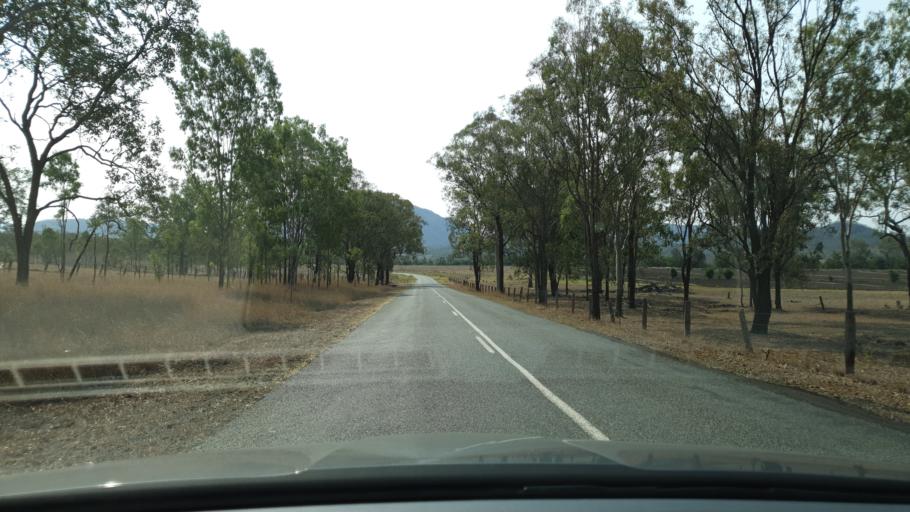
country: AU
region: Queensland
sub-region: Logan
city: Cedar Vale
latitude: -28.1401
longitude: 152.6040
